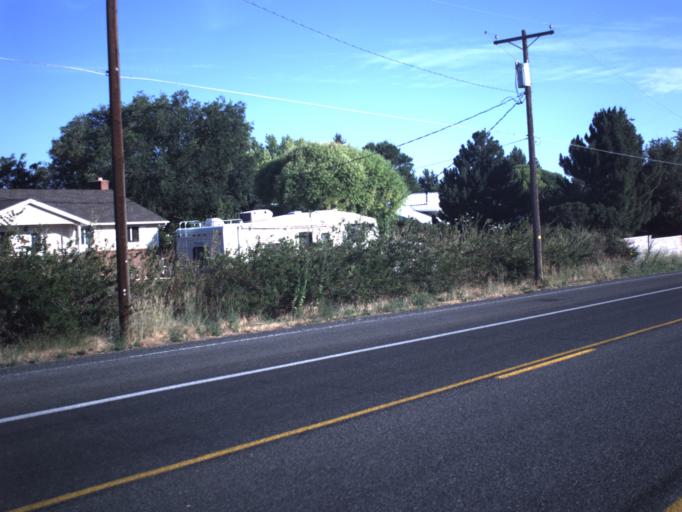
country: US
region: Utah
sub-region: Iron County
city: Enoch
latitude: 37.7460
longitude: -113.0552
